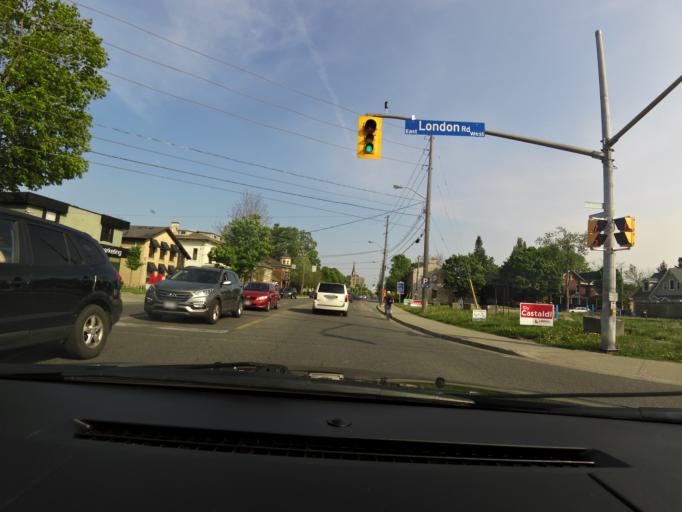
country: CA
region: Ontario
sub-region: Wellington County
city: Guelph
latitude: 43.5501
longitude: -80.2569
